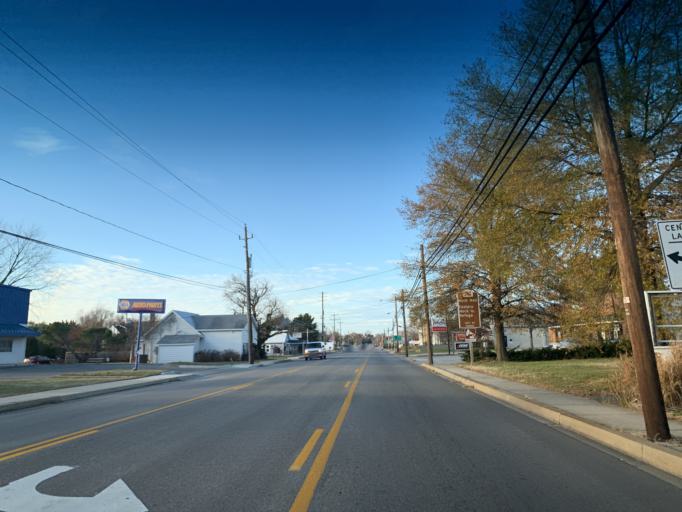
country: US
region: Maryland
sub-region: Kent County
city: Chestertown
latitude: 39.2210
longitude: -76.0683
